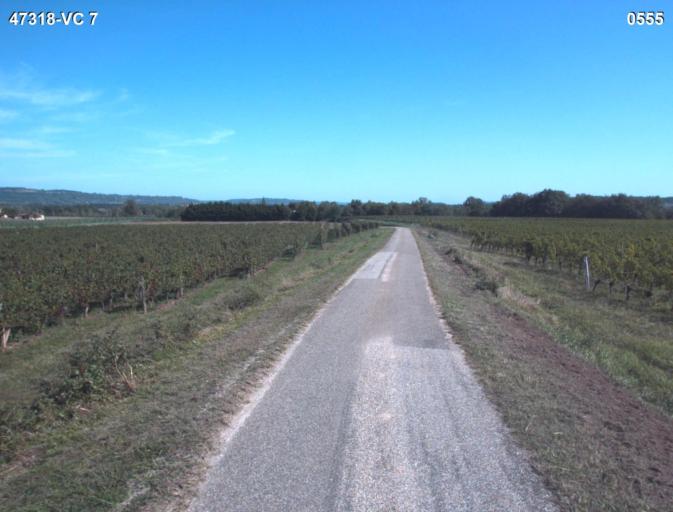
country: FR
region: Aquitaine
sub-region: Departement du Lot-et-Garonne
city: Buzet-sur-Baise
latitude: 44.2301
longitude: 0.3168
